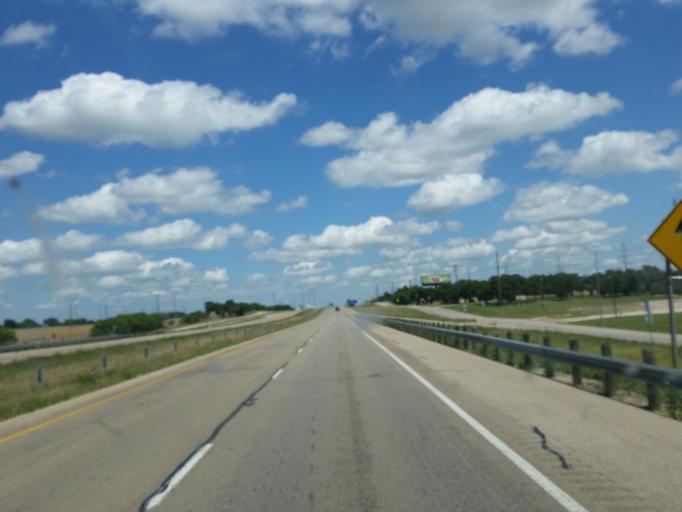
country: US
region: Texas
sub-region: Callahan County
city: Clyde
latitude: 32.4180
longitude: -99.5245
